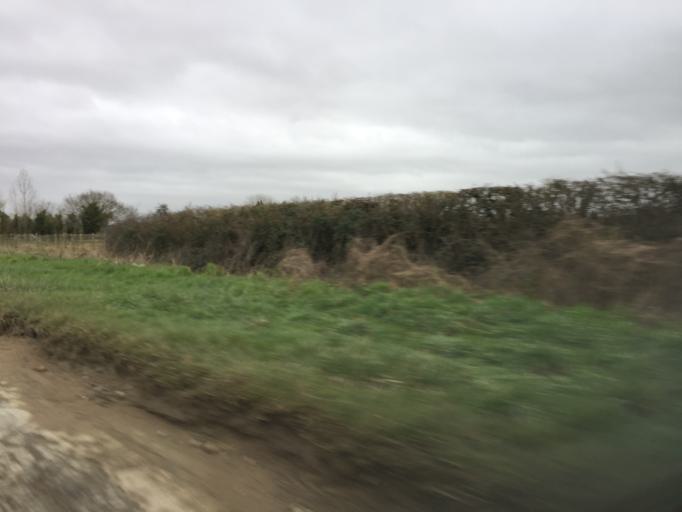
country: GB
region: England
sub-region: Oxfordshire
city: Stanford in the Vale
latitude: 51.6455
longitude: -1.5356
